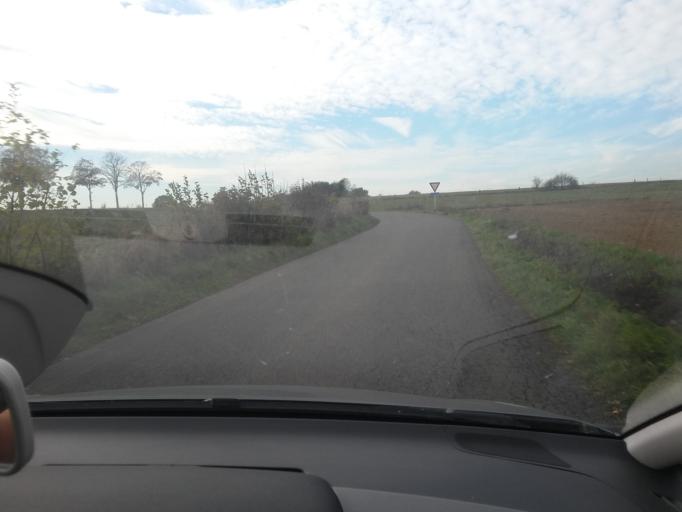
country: BE
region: Wallonia
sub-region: Province du Luxembourg
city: Attert
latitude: 49.7072
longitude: 5.7157
